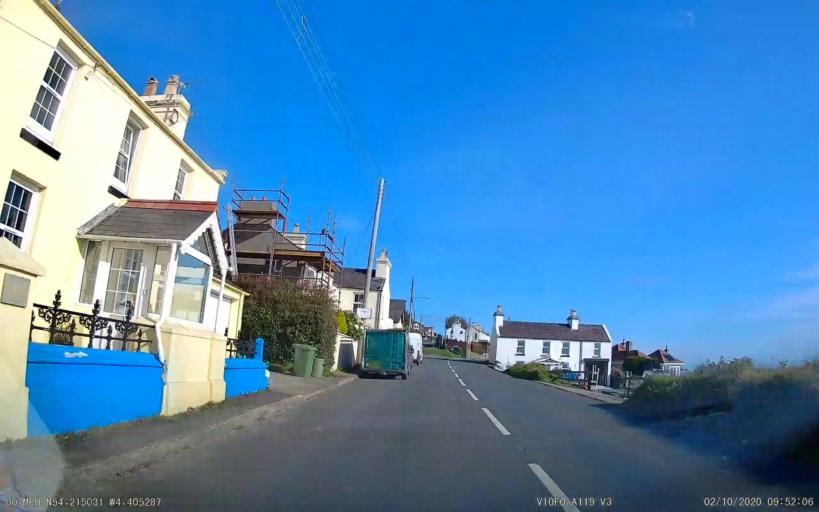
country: IM
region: Laxey
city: Laxey
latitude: 54.2150
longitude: -4.4053
